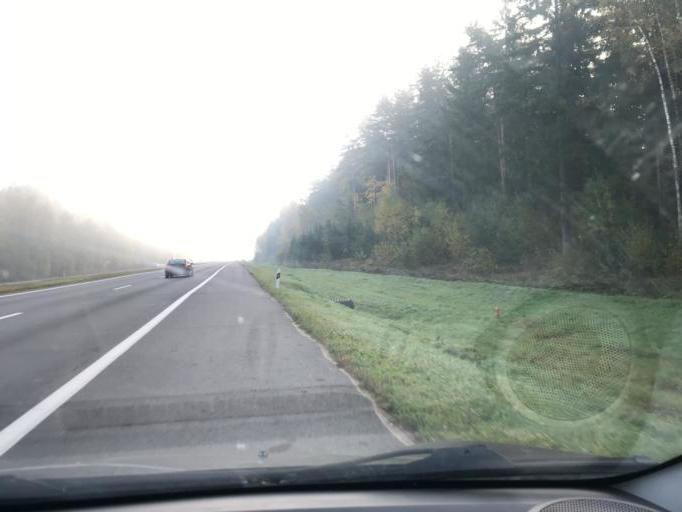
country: BY
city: Michanovichi
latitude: 53.7731
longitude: 27.6923
